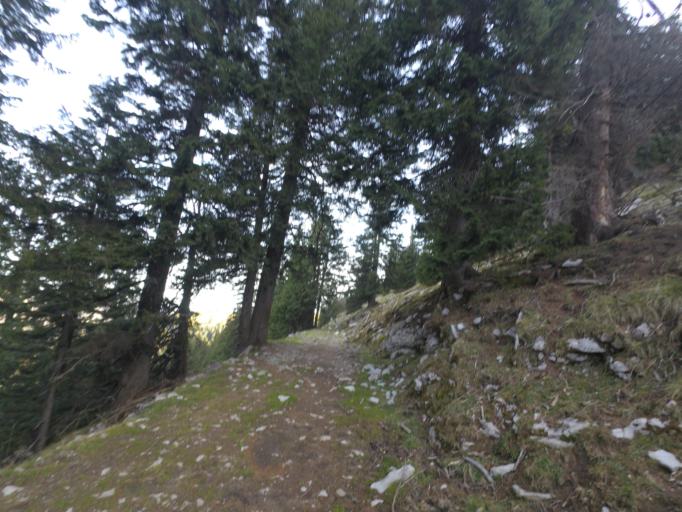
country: AT
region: Salzburg
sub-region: Politischer Bezirk Salzburg-Umgebung
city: Hintersee
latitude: 47.6416
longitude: 13.2689
